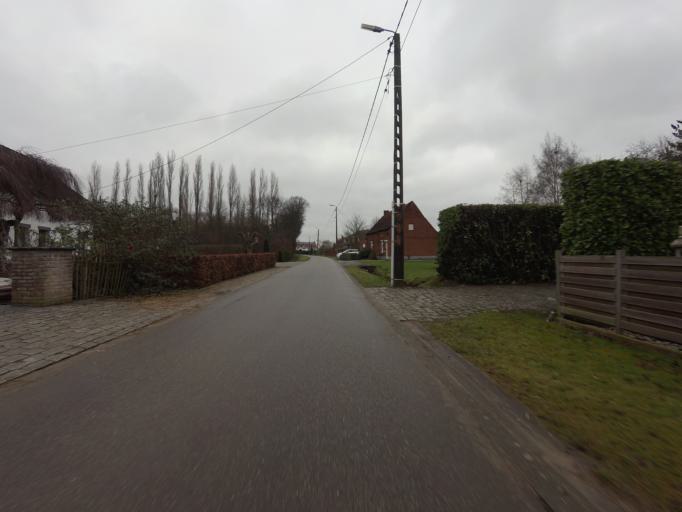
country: BE
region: Flanders
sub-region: Provincie Antwerpen
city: Sint-Katelijne-Waver
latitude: 51.0471
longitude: 4.5450
